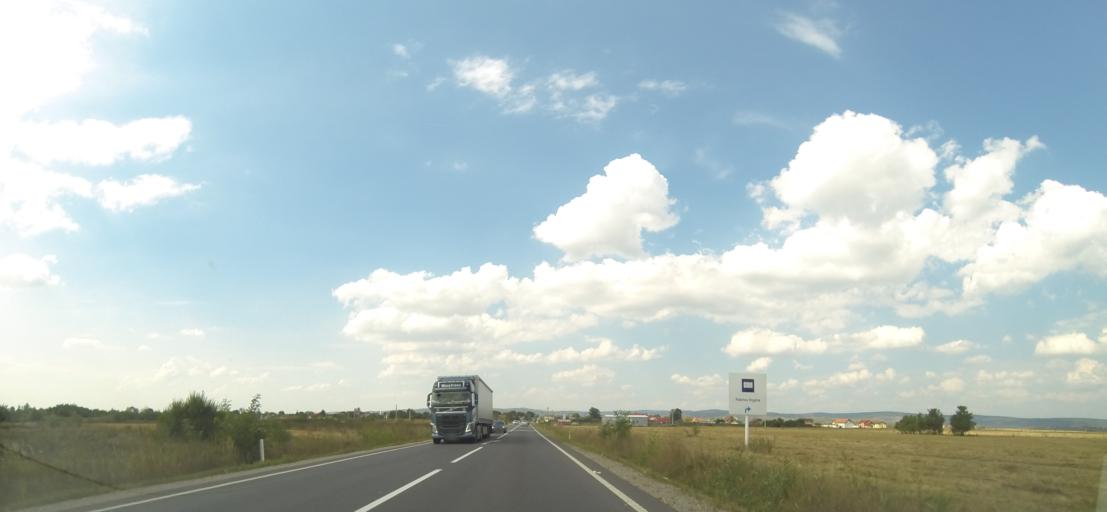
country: RO
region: Brasov
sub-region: Comuna Sercaia
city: Sercaia
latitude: 45.8262
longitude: 25.1533
